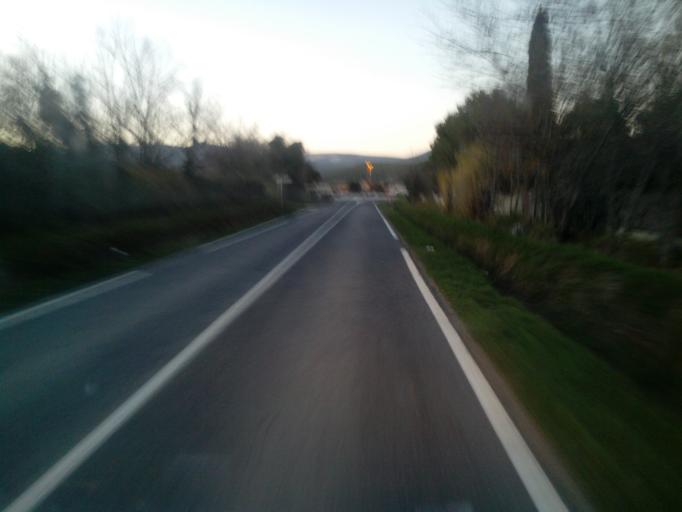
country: FR
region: Languedoc-Roussillon
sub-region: Departement des Pyrenees-Orientales
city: Peyrestortes
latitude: 42.7762
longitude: 2.8287
